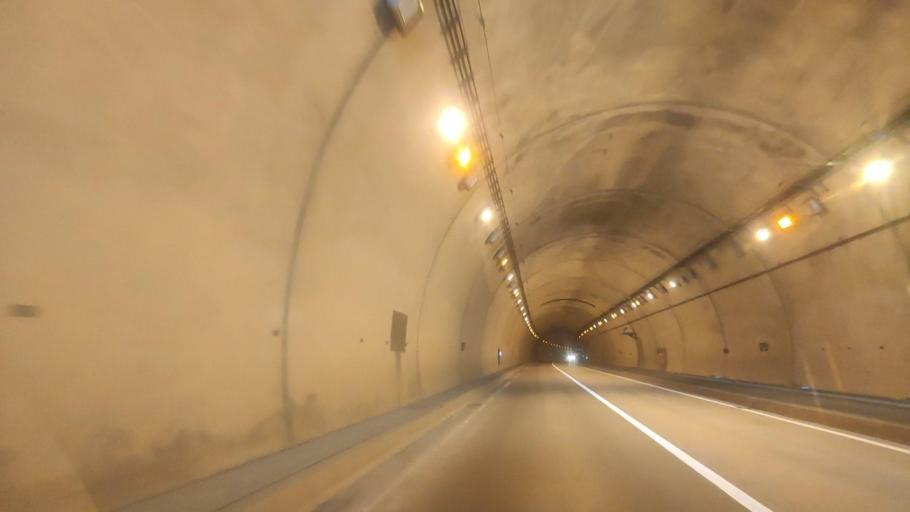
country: JP
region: Hokkaido
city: Date
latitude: 42.5604
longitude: 140.7795
